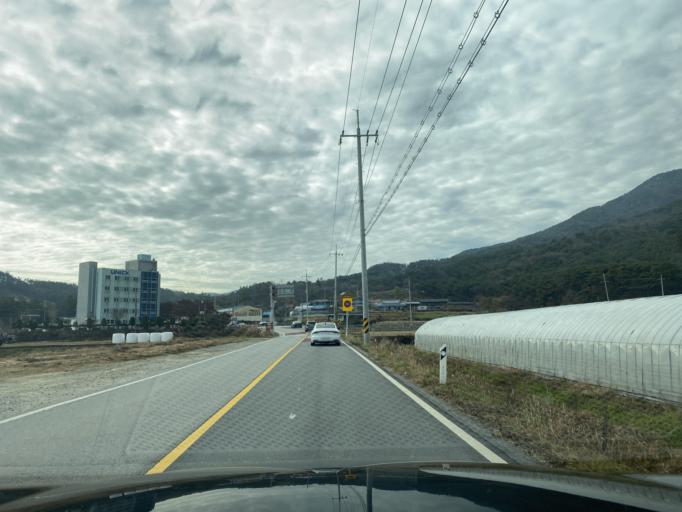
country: KR
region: Chungcheongnam-do
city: Hongsung
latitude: 36.6765
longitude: 126.6434
